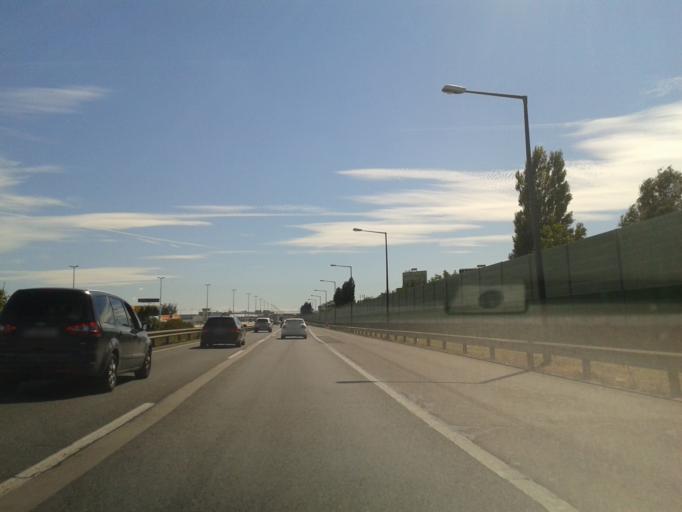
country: AT
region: Lower Austria
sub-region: Politischer Bezirk Modling
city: Vosendorf
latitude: 48.1441
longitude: 16.3349
